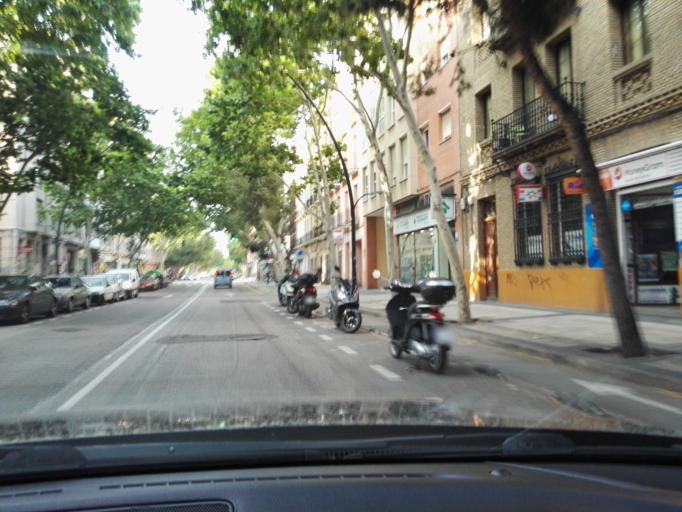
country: ES
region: Aragon
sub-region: Provincia de Zaragoza
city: Zaragoza
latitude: 41.6595
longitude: -0.8742
